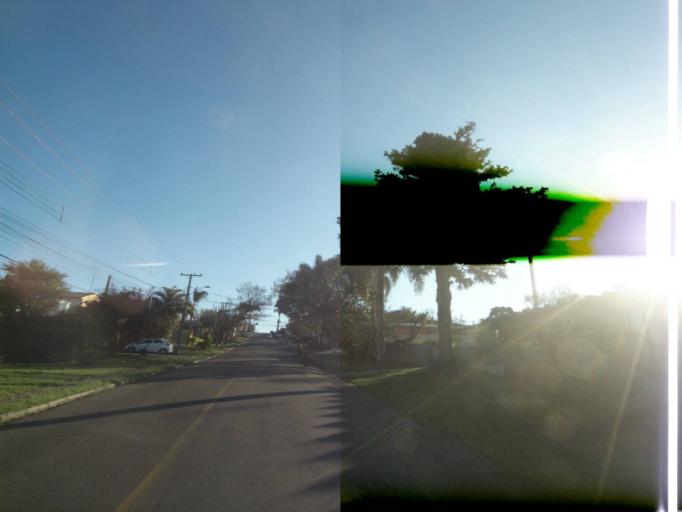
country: BR
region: Parana
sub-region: Curitiba
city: Curitiba
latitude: -25.3814
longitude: -49.2509
